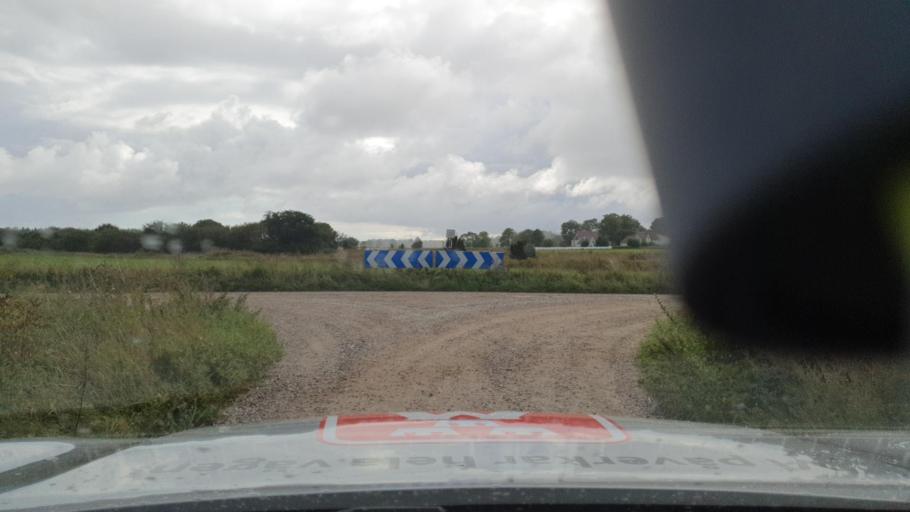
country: SE
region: Gotland
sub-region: Gotland
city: Hemse
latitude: 56.9992
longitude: 18.3242
